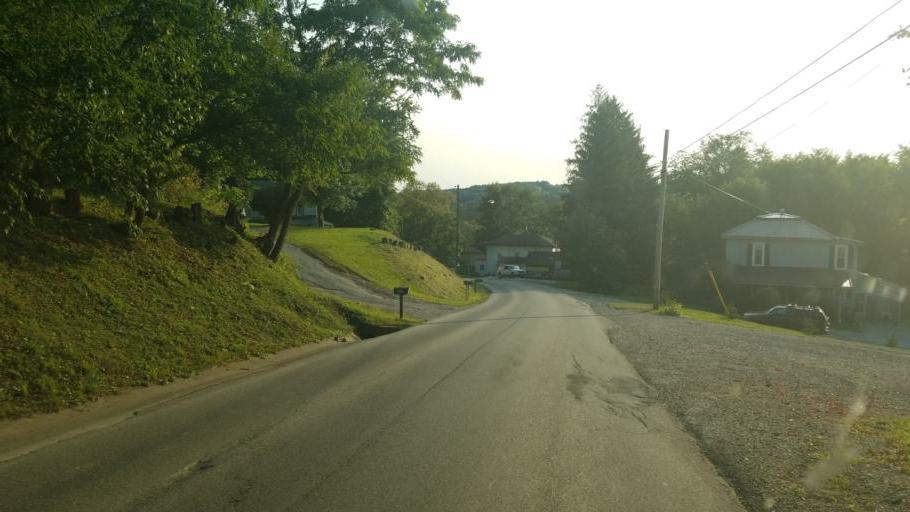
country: US
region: Ohio
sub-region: Wayne County
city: Apple Creek
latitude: 40.6787
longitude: -81.8676
